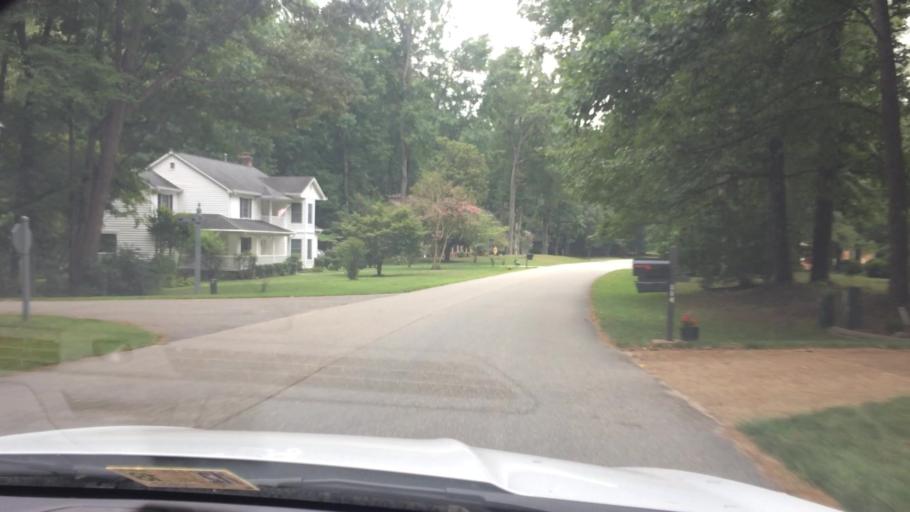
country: US
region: Virginia
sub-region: James City County
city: Williamsburg
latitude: 37.3091
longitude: -76.7719
